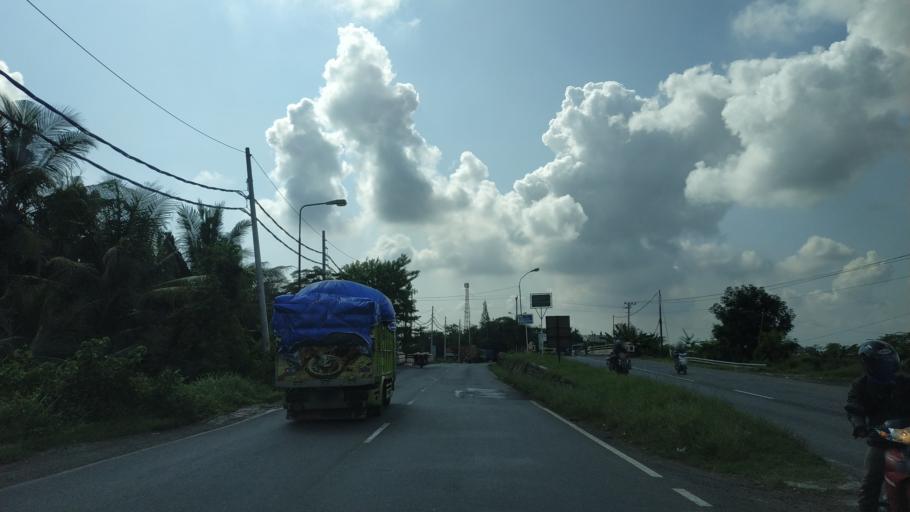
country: ID
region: Central Java
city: Wiradesa
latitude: -6.8883
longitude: 109.5817
